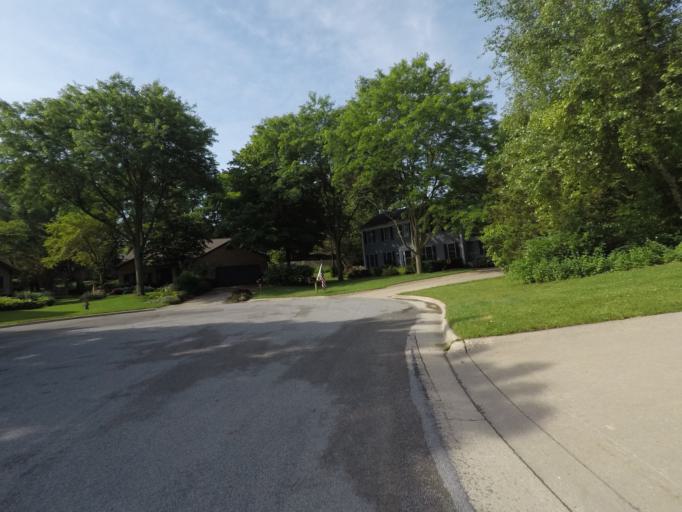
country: US
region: Wisconsin
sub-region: Dane County
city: Middleton
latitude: 43.0766
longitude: -89.4957
